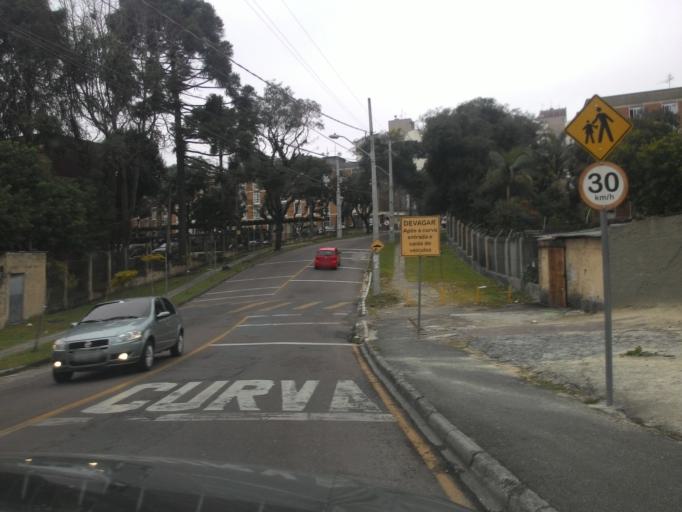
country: BR
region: Parana
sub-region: Curitiba
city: Curitiba
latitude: -25.4818
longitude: -49.2881
